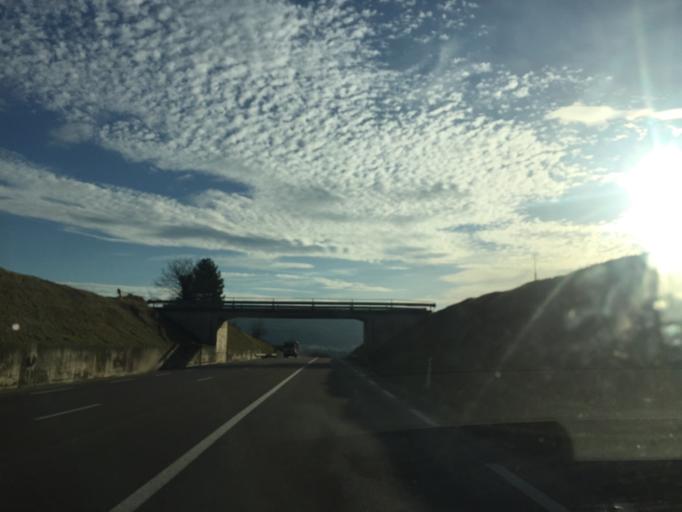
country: FR
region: Franche-Comte
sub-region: Departement du Jura
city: Arbois
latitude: 46.9304
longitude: 5.7758
